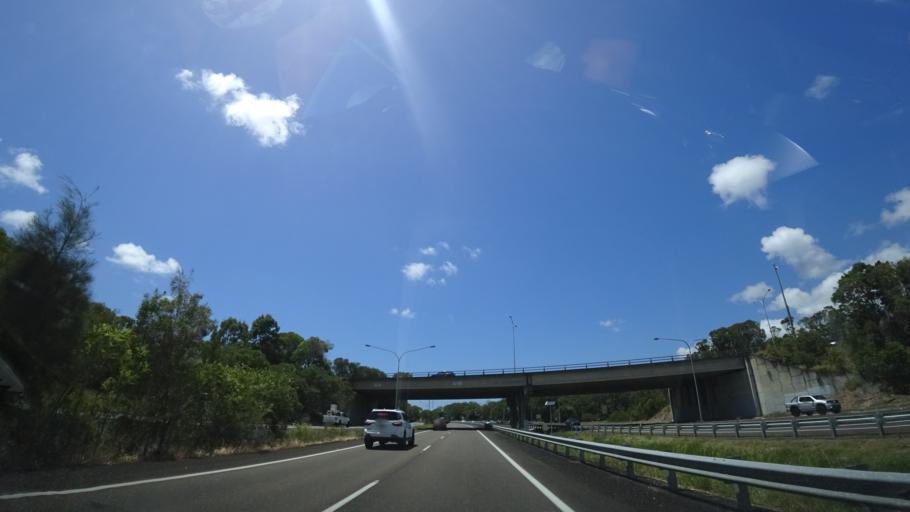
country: AU
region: Queensland
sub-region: Sunshine Coast
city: Mooloolaba
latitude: -26.6934
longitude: 153.1113
